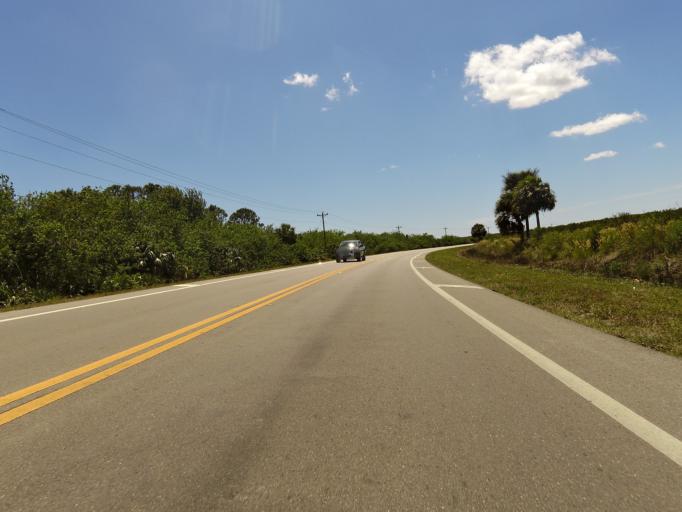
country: US
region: Florida
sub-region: Collier County
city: Immokalee
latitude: 26.3690
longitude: -81.4194
